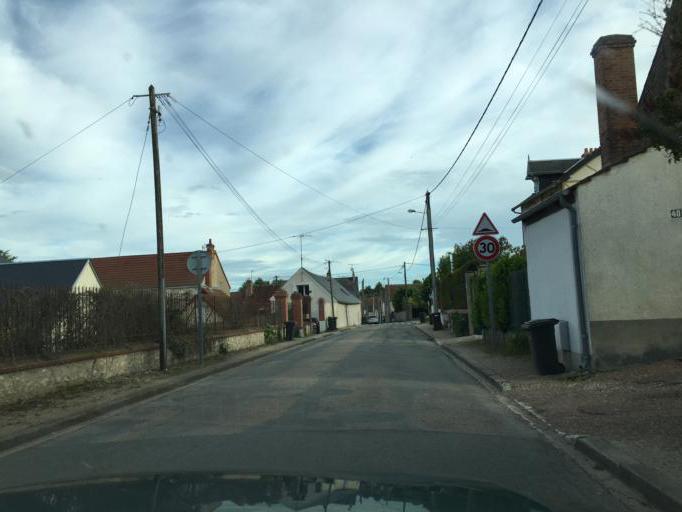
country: FR
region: Centre
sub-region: Departement du Loiret
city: Saint-Ay
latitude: 47.8638
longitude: 1.7480
